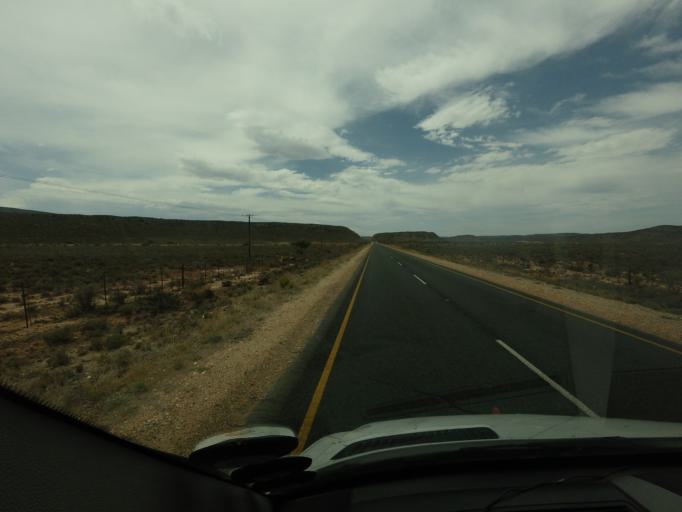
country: ZA
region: Western Cape
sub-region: Eden District Municipality
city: Riversdale
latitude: -33.8325
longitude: 20.8806
